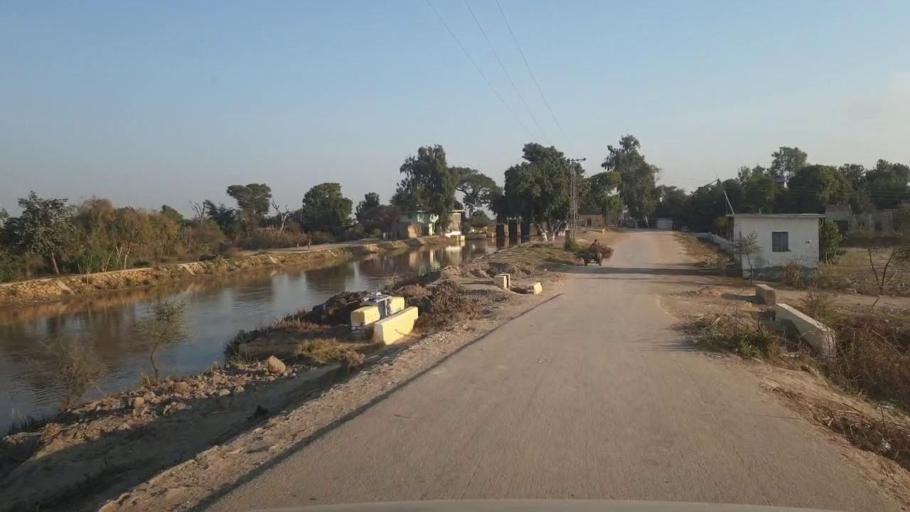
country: PK
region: Sindh
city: Chambar
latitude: 25.2964
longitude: 68.8915
